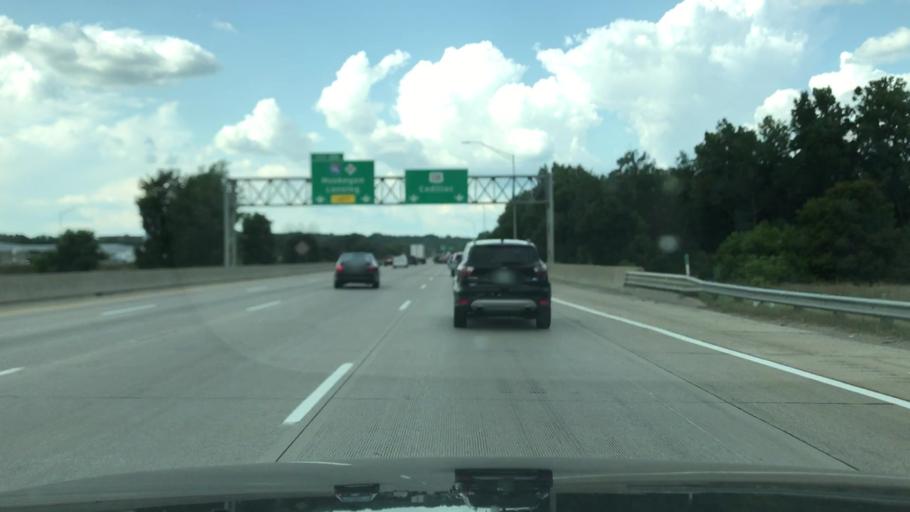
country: US
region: Michigan
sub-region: Kent County
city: Comstock Park
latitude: 43.0021
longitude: -85.6753
